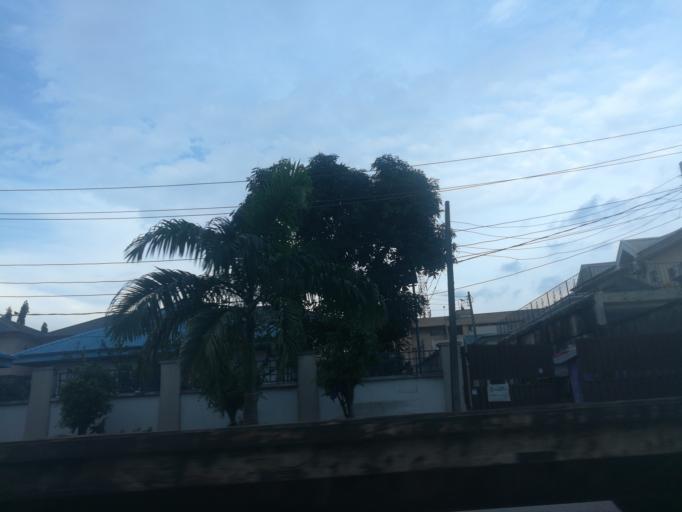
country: NG
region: Lagos
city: Somolu
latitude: 6.5507
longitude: 3.3896
